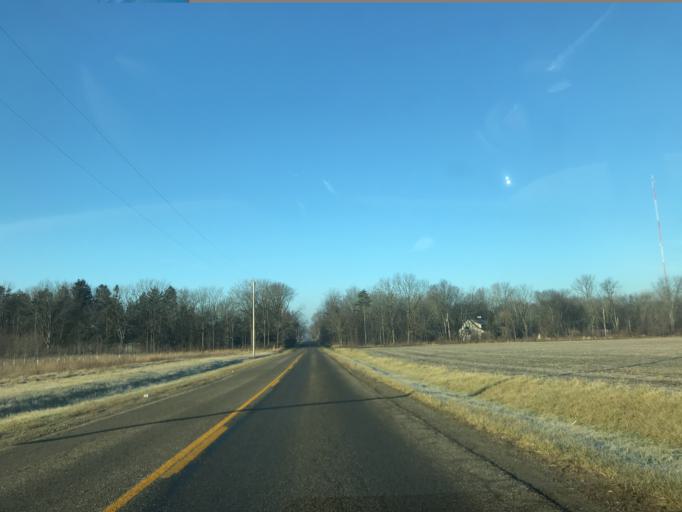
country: US
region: Michigan
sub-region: Eaton County
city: Dimondale
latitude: 42.6621
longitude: -84.6054
